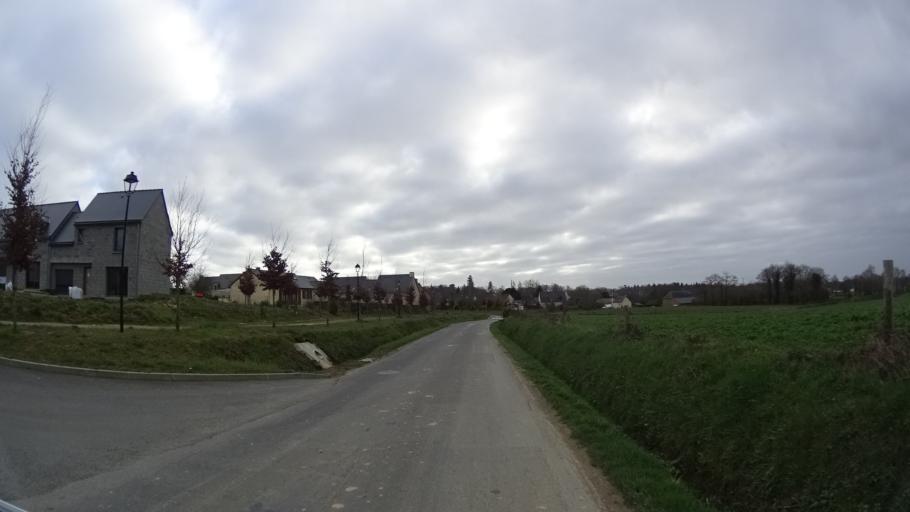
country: FR
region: Brittany
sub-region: Departement d'Ille-et-Vilaine
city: Saint-Gilles
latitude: 48.1773
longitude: -1.8595
